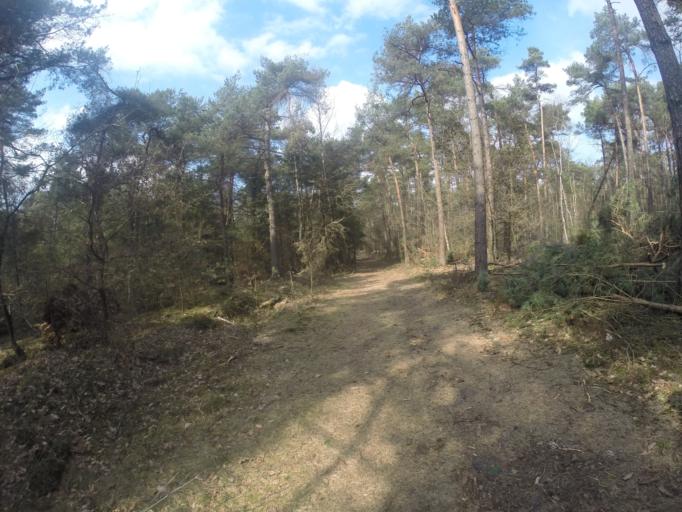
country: NL
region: Gelderland
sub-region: Gemeente Lochem
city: Almen
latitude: 52.1325
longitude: 6.3228
